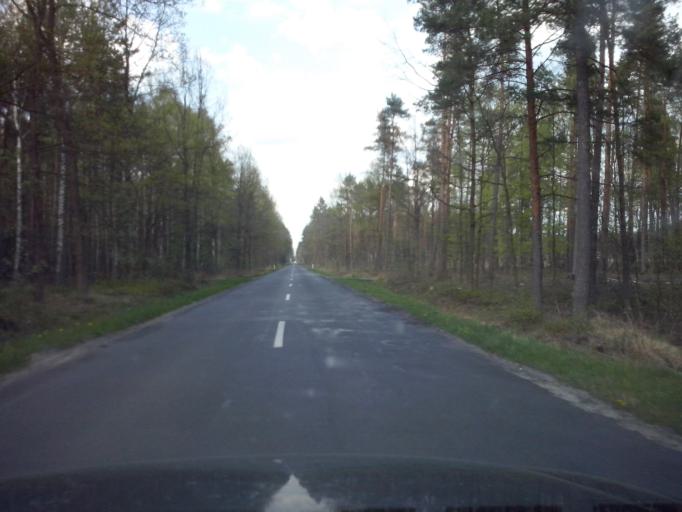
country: PL
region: Subcarpathian Voivodeship
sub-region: Powiat lezajski
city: Letownia
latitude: 50.3679
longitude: 22.2478
